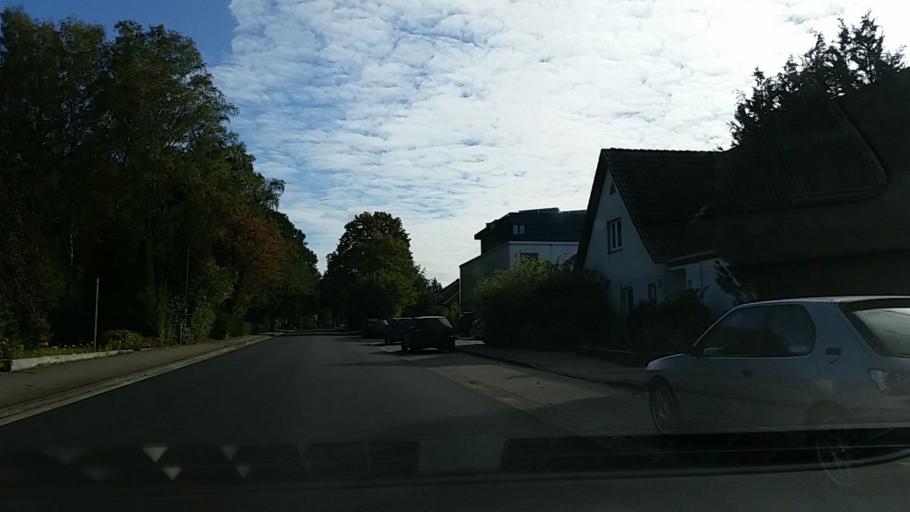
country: DE
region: Lower Saxony
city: Neuenkirchen
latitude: 53.0312
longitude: 9.7098
